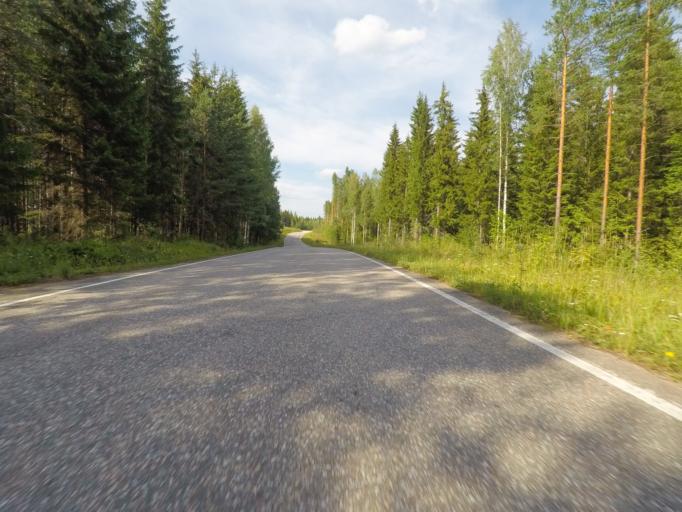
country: FI
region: Southern Savonia
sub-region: Savonlinna
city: Sulkava
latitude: 61.7739
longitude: 28.2391
